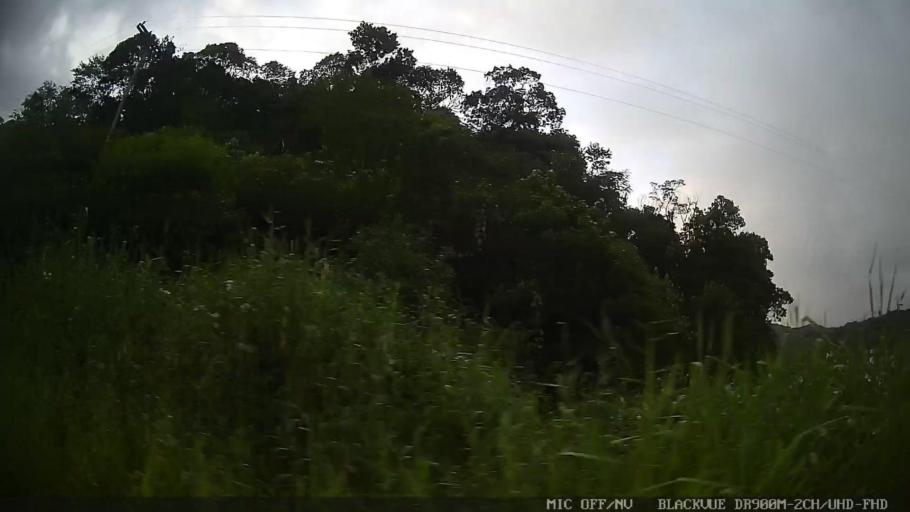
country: BR
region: Sao Paulo
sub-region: Itanhaem
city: Itanhaem
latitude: -24.0860
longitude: -46.8000
